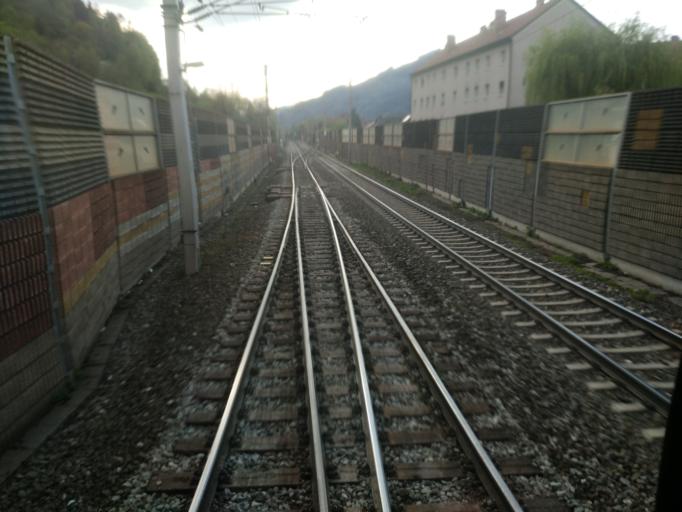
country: AT
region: Styria
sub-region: Politischer Bezirk Bruck-Muerzzuschlag
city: Bruck an der Mur
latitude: 47.4058
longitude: 15.2710
